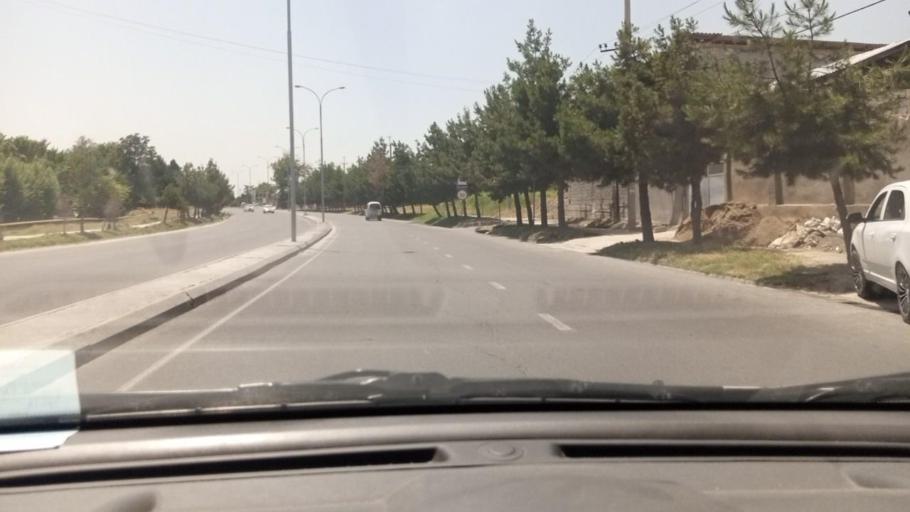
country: UZ
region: Toshkent
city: Urtaowul
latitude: 41.2217
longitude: 69.1759
